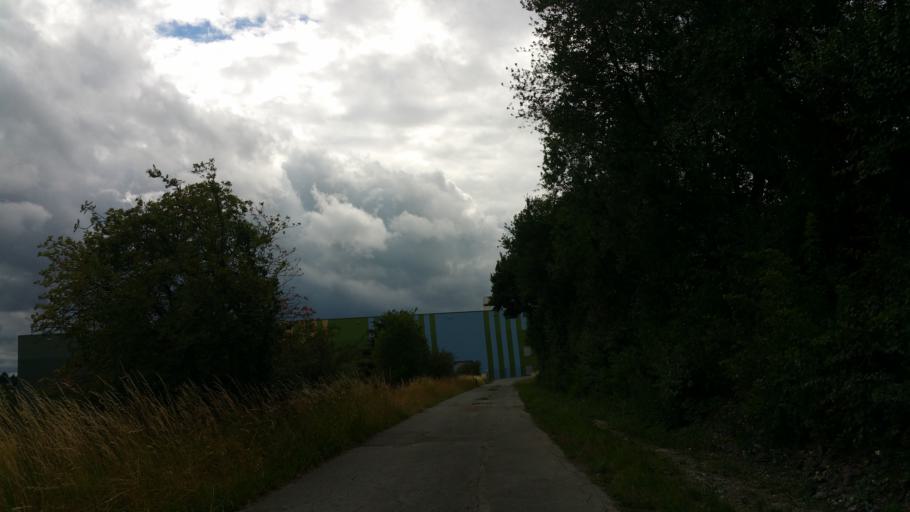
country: DE
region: Bavaria
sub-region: Upper Franconia
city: Schwarzenbach an der Saale
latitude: 50.2246
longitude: 11.9624
